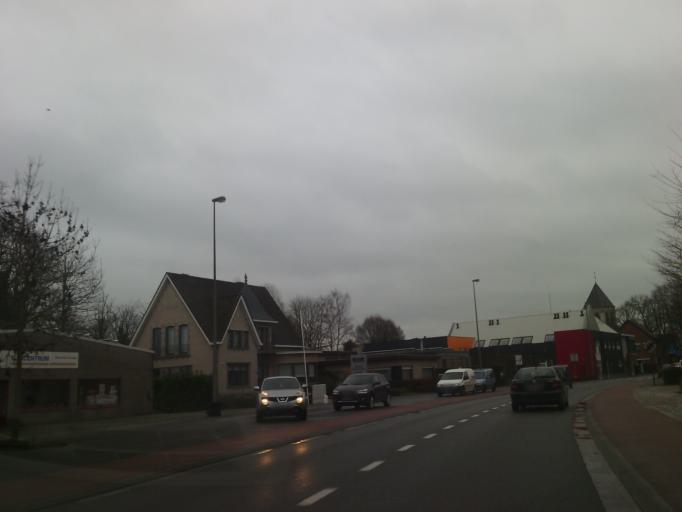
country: BE
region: Flanders
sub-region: Provincie Oost-Vlaanderen
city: Berlare
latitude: 51.0267
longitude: 4.0015
